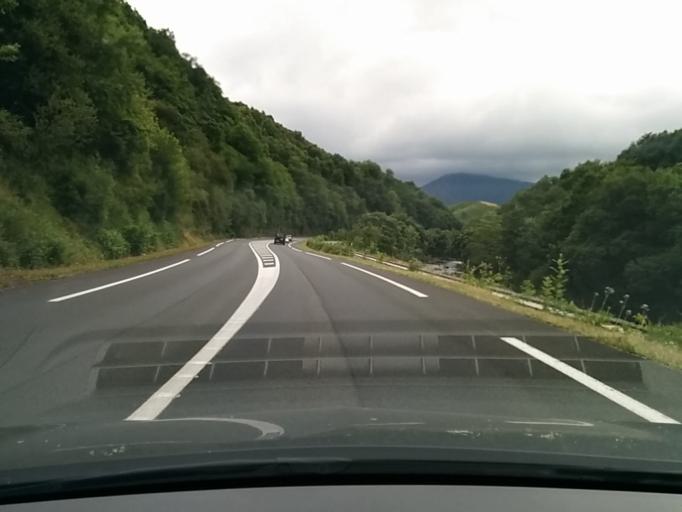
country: FR
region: Aquitaine
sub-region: Departement des Pyrenees-Atlantiques
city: Itxassou
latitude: 43.2983
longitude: -1.3501
